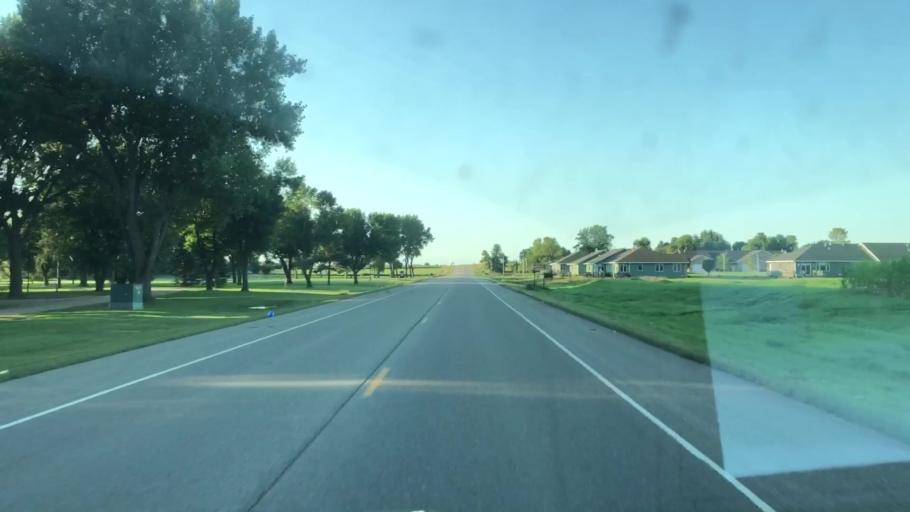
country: US
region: Minnesota
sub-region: Nobles County
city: Worthington
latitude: 43.6087
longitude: -95.6366
